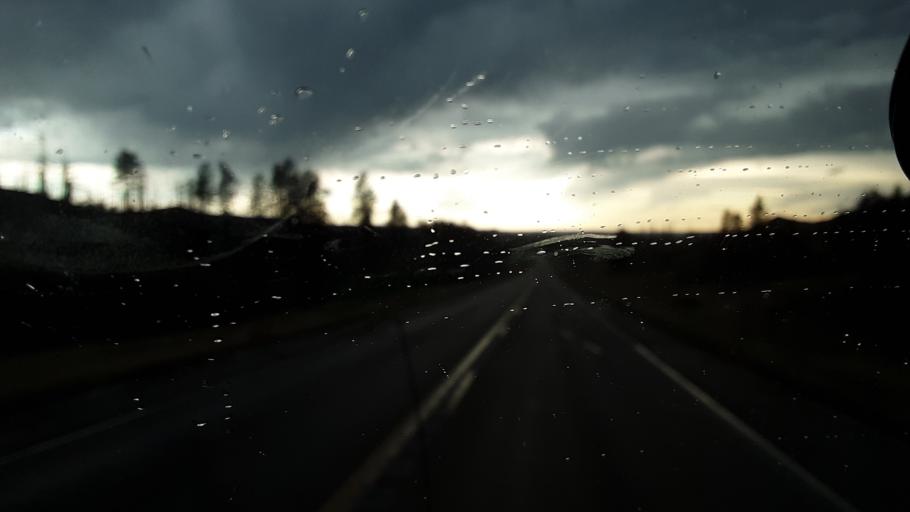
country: US
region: Montana
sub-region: Powder River County
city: Broadus
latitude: 45.5525
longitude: -105.9002
